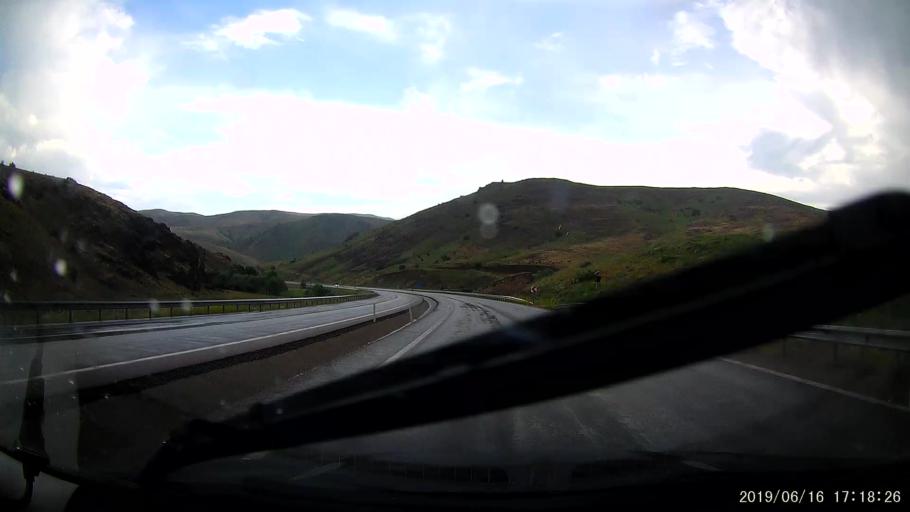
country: TR
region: Erzincan
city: Tercan
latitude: 39.8143
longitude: 40.5287
